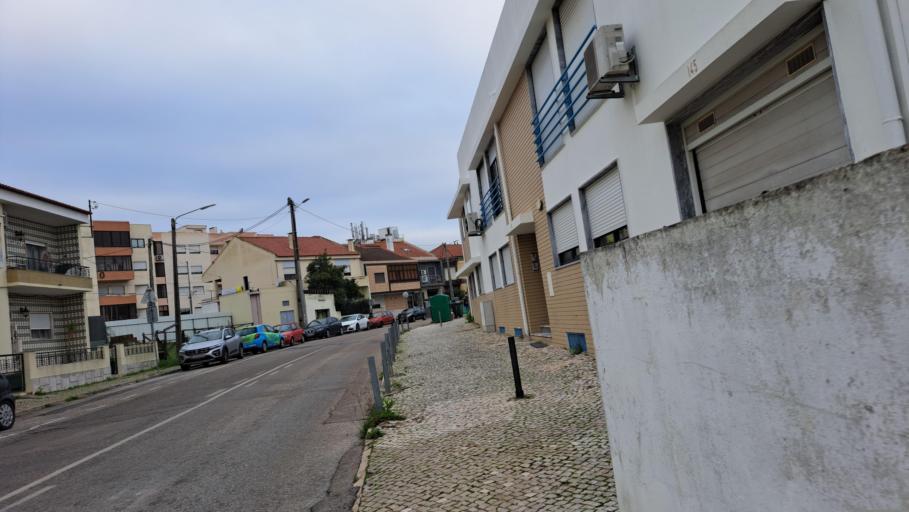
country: PT
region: Setubal
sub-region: Moita
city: Alhos Vedros
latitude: 38.6523
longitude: -9.0464
